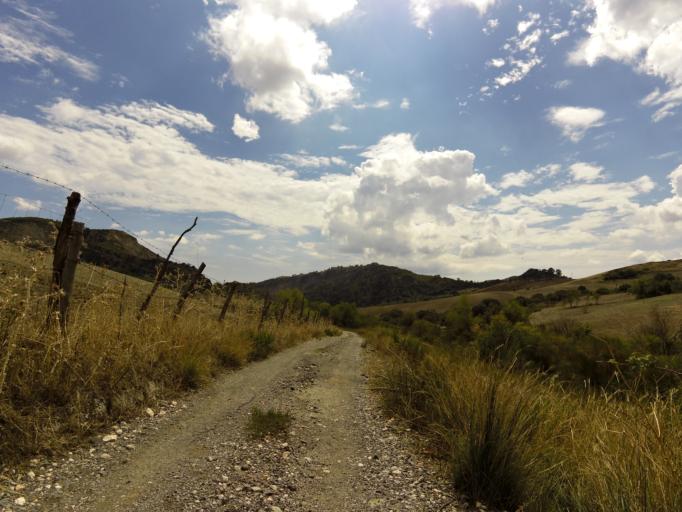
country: IT
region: Calabria
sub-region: Provincia di Reggio Calabria
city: Stilo
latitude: 38.4558
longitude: 16.4650
